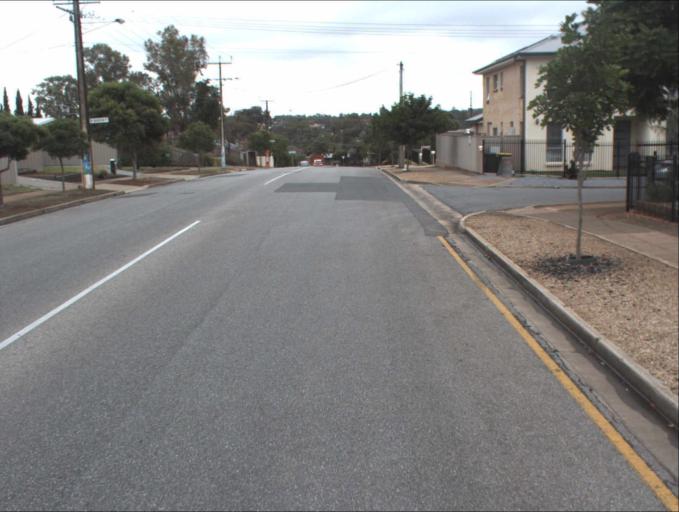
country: AU
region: South Australia
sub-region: Port Adelaide Enfield
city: Gilles Plains
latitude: -34.8476
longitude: 138.6599
